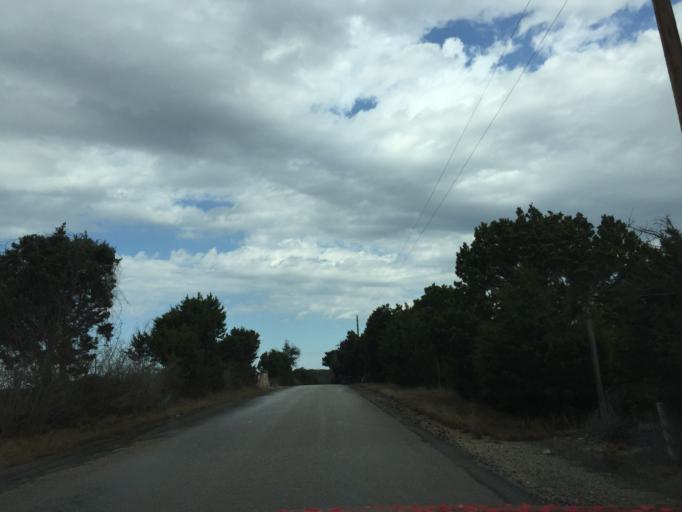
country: US
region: Texas
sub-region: Burnet County
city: Bertram
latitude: 30.6361
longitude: -98.0067
